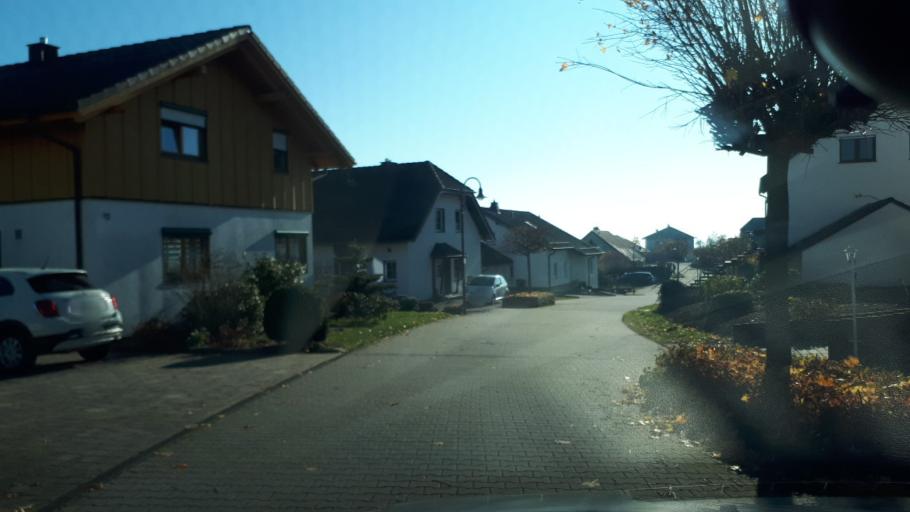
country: DE
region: Rheinland-Pfalz
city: Illerich
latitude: 50.1994
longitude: 7.1849
